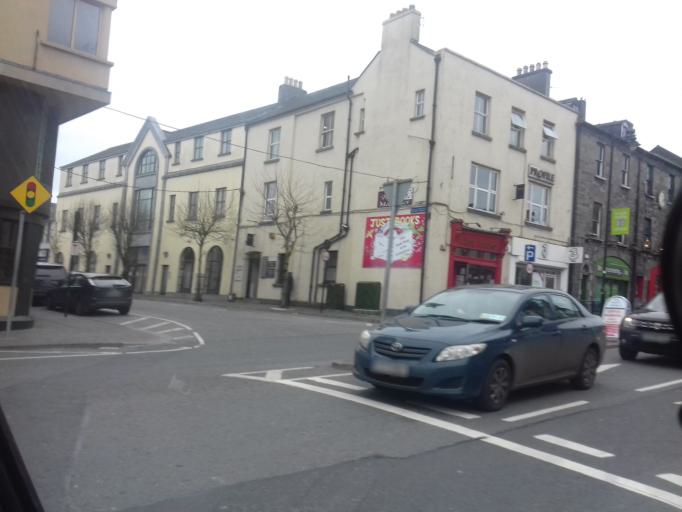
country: IE
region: Leinster
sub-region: An Iarmhi
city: An Muileann gCearr
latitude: 53.5260
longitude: -7.3397
